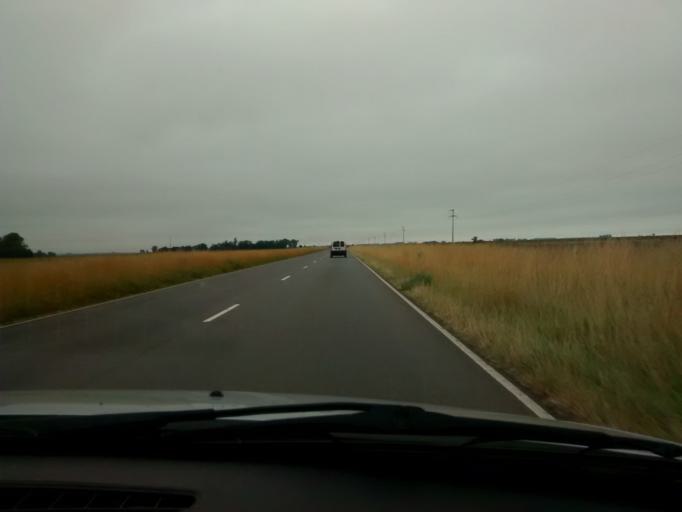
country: AR
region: Buenos Aires
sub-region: Partido de Ayacucho
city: Ayacucho
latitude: -37.0439
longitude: -58.5413
